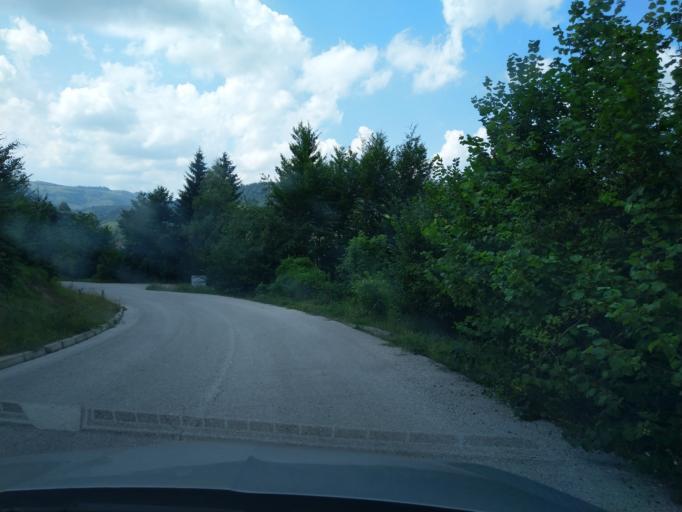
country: RS
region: Central Serbia
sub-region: Zlatiborski Okrug
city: Nova Varos
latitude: 43.5794
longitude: 19.8860
